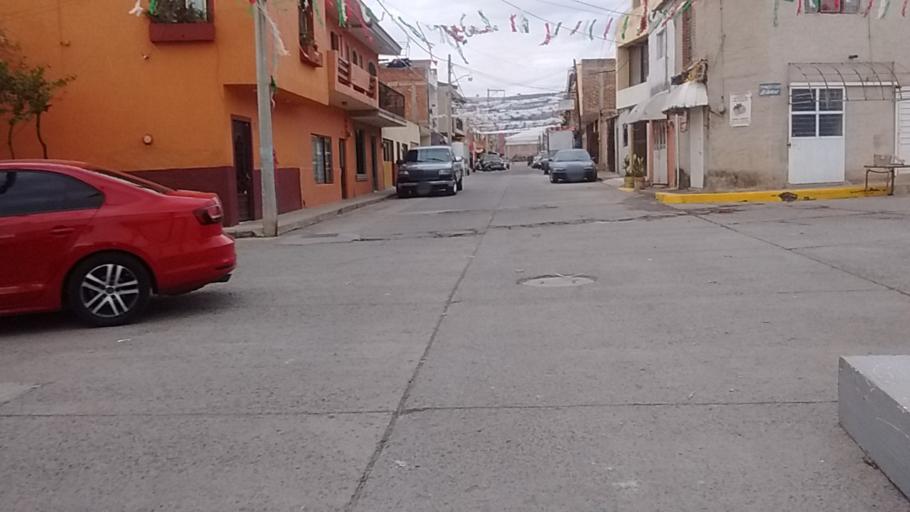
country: MX
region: Jalisco
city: Atotonilco el Alto
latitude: 20.5439
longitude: -102.5129
